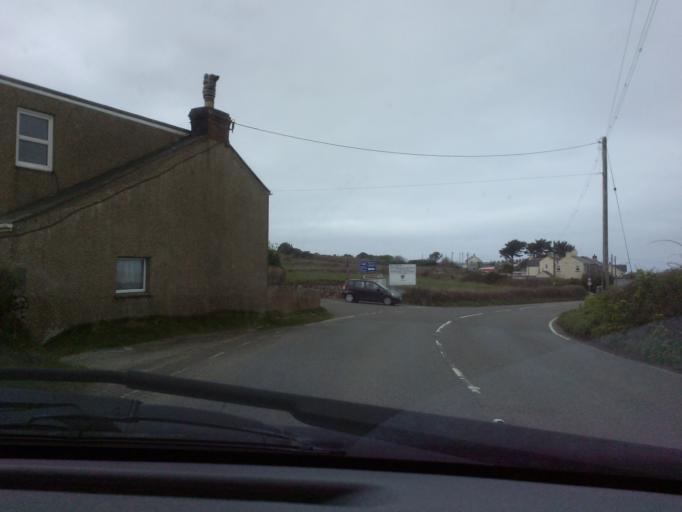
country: GB
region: England
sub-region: Cornwall
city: Saint Just
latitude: 50.1209
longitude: -5.6741
